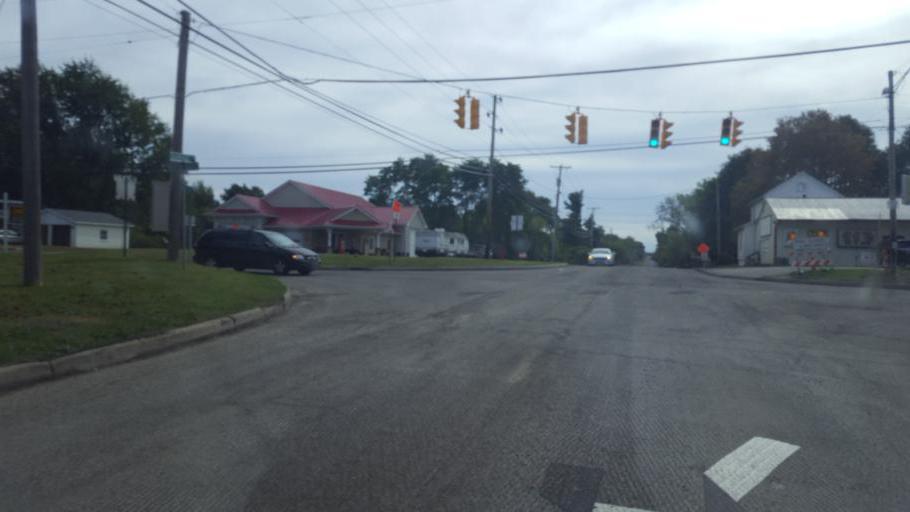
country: US
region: Ohio
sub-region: Lorain County
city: South Amherst
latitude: 41.3893
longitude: -82.2825
